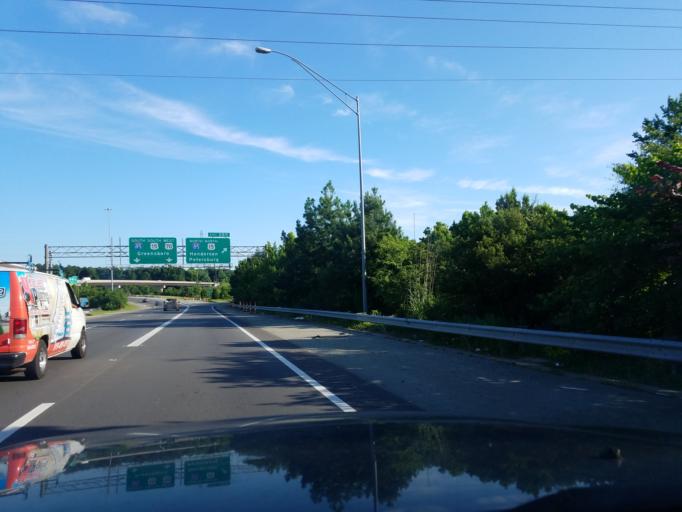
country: US
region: North Carolina
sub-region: Durham County
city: Durham
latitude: 36.0107
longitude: -78.8677
